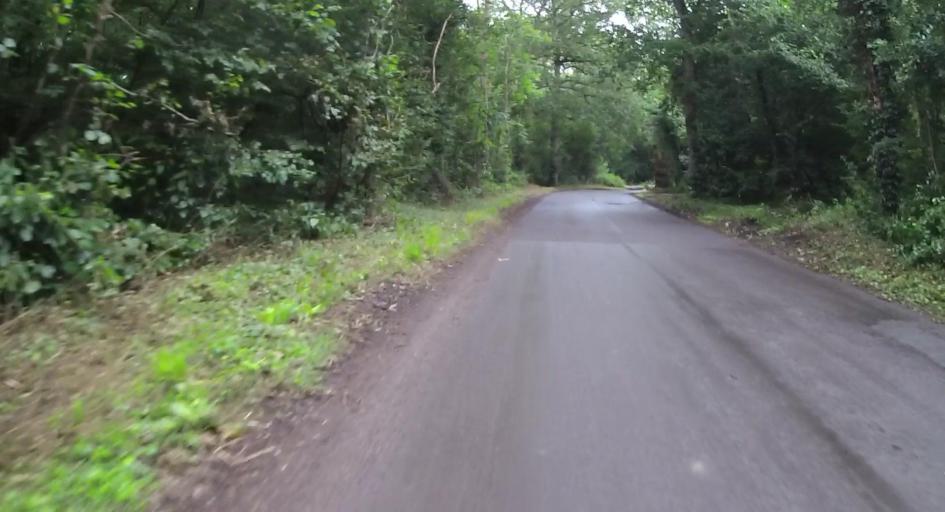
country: GB
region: England
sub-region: Hampshire
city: Andover
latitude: 51.1999
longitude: -1.4026
